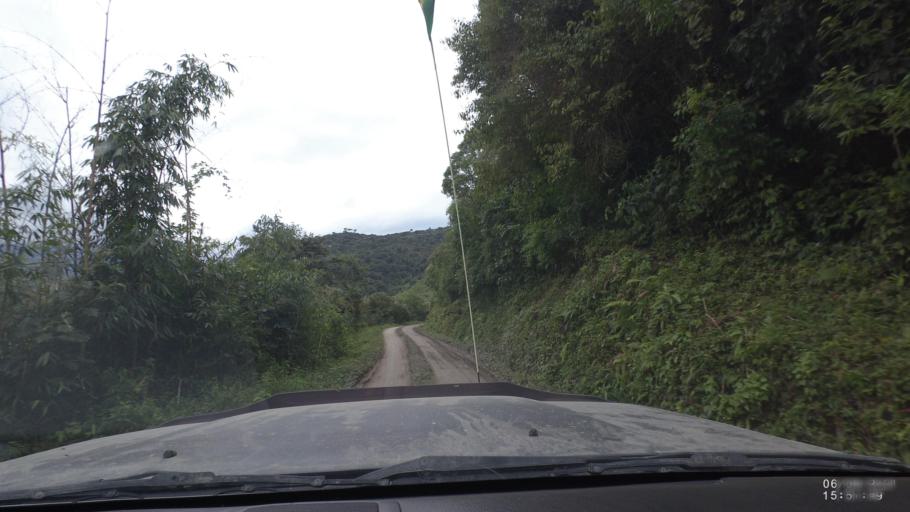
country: BO
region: La Paz
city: Quime
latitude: -16.5876
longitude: -66.7089
